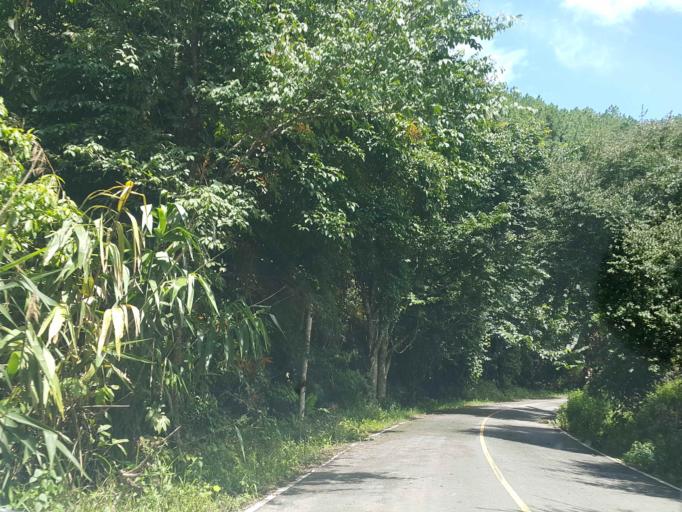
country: TH
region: Chiang Mai
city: Mae Chaem
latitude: 18.5220
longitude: 98.5218
